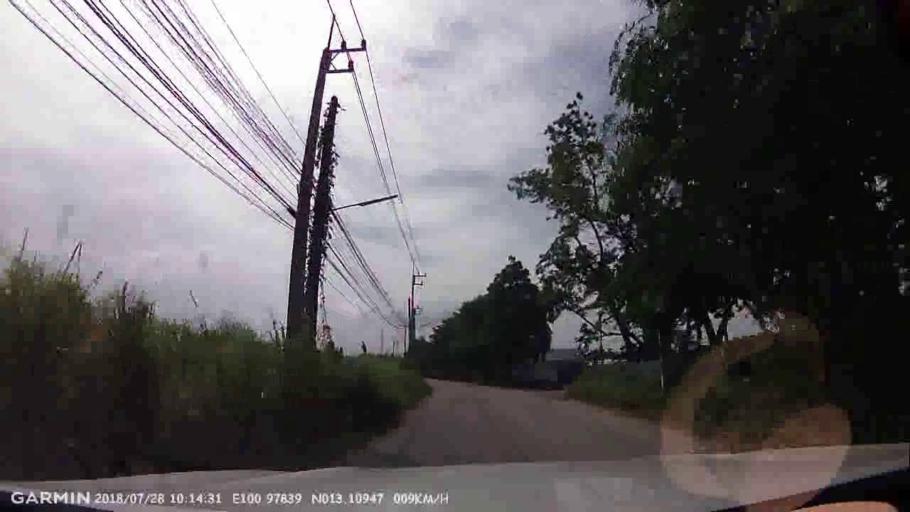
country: TH
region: Chon Buri
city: Ban Talat Bueng
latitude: 13.1094
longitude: 100.9785
